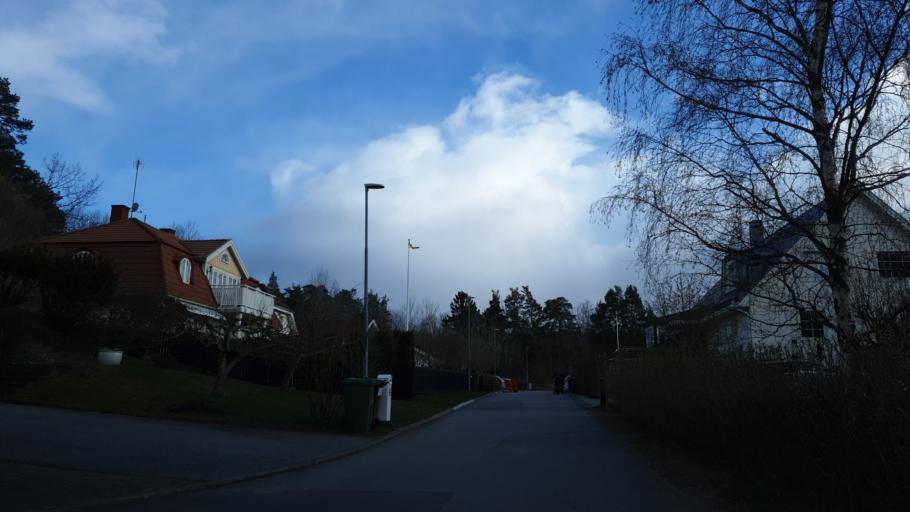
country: SE
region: Stockholm
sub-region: Lidingo
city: Lidingoe
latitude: 59.3901
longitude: 18.1206
